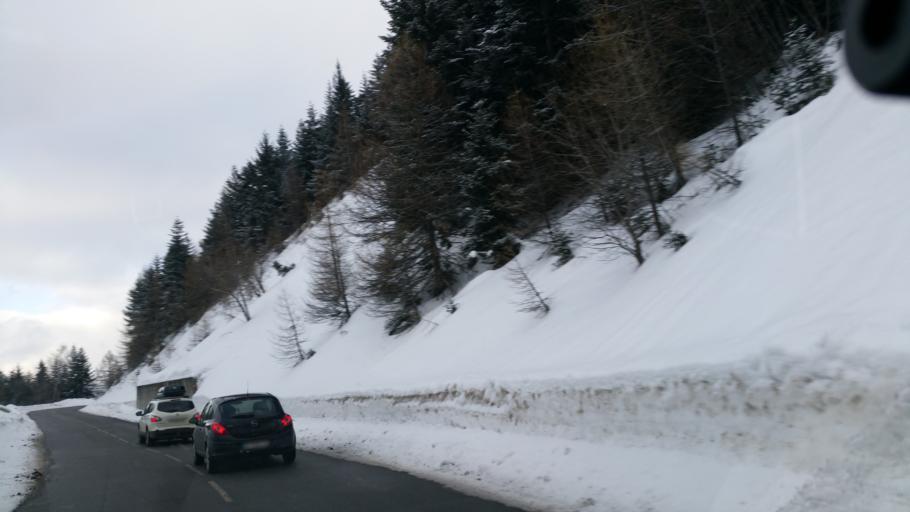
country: FR
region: Rhone-Alpes
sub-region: Departement de la Savoie
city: Villargondran
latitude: 45.2353
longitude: 6.3965
